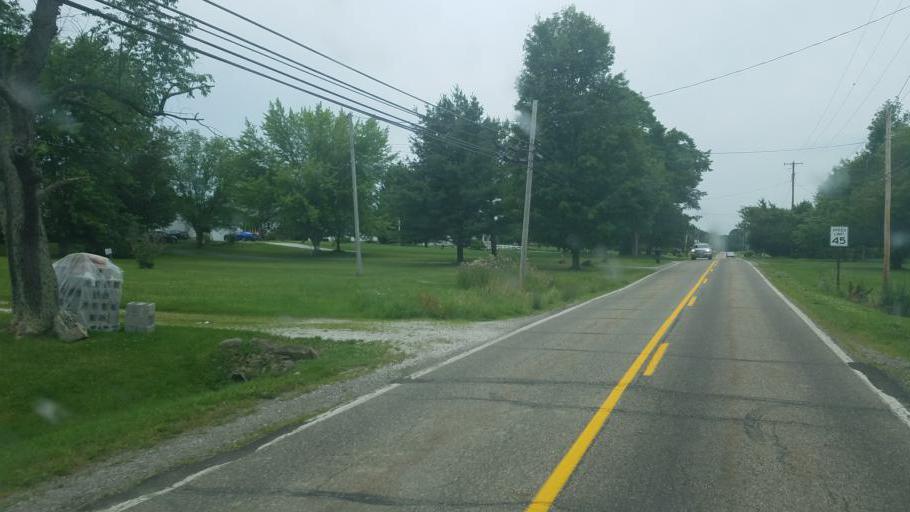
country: US
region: Ohio
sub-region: Portage County
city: Ravenna
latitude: 41.0990
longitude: -81.1705
